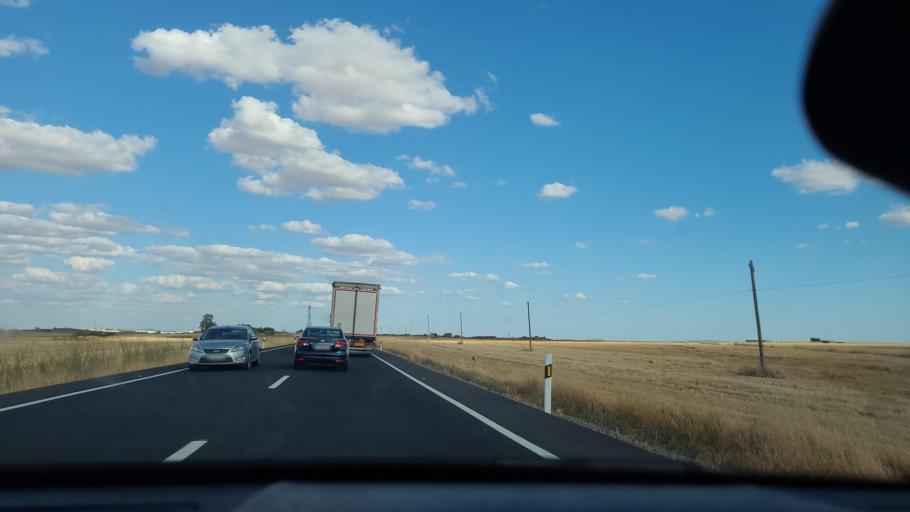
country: ES
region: Extremadura
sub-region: Provincia de Badajoz
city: Azuaga
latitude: 38.2626
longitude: -5.7336
